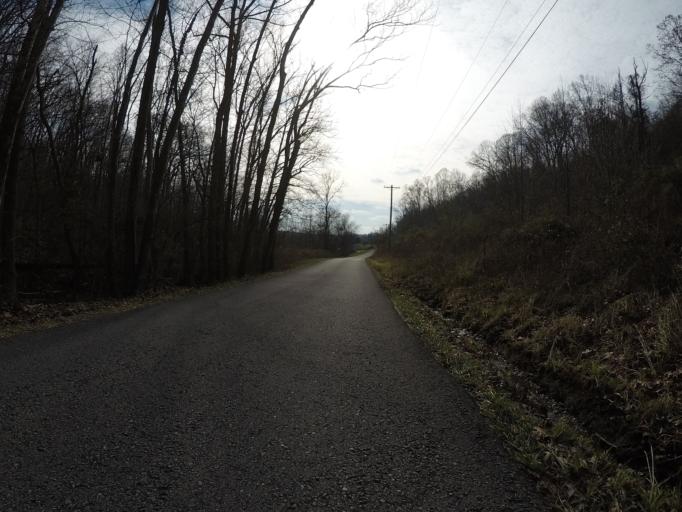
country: US
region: West Virginia
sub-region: Cabell County
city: Pea Ridge
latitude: 38.4256
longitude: -82.3408
